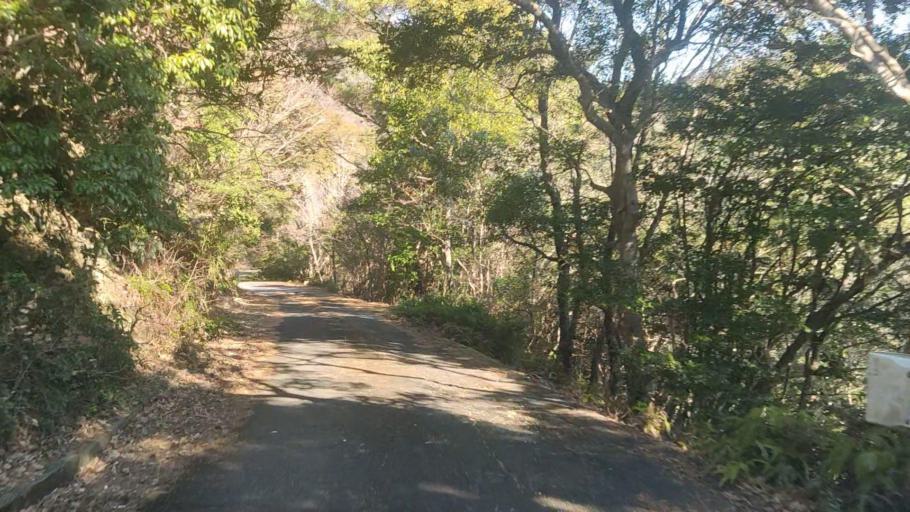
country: JP
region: Oita
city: Saiki
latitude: 32.7825
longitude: 131.8514
